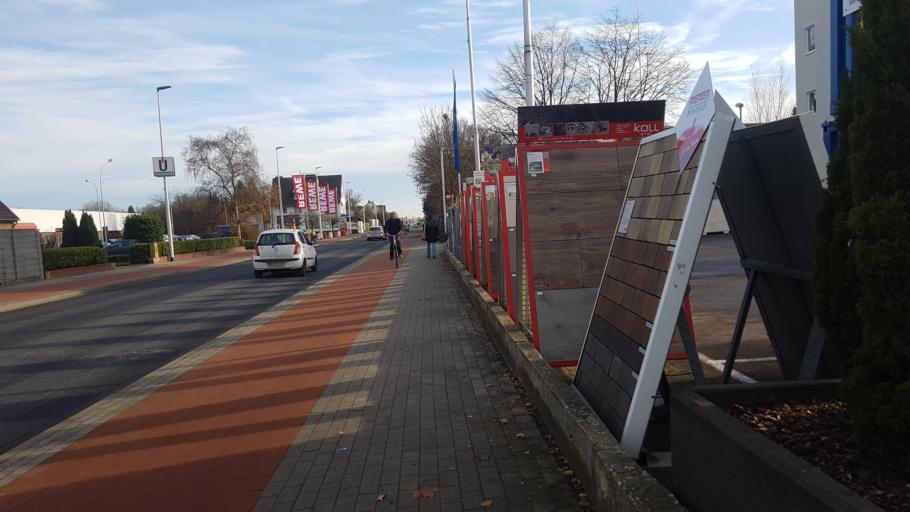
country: DE
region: North Rhine-Westphalia
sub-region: Regierungsbezirk Koln
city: Heinsberg
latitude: 51.0648
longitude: 6.1029
